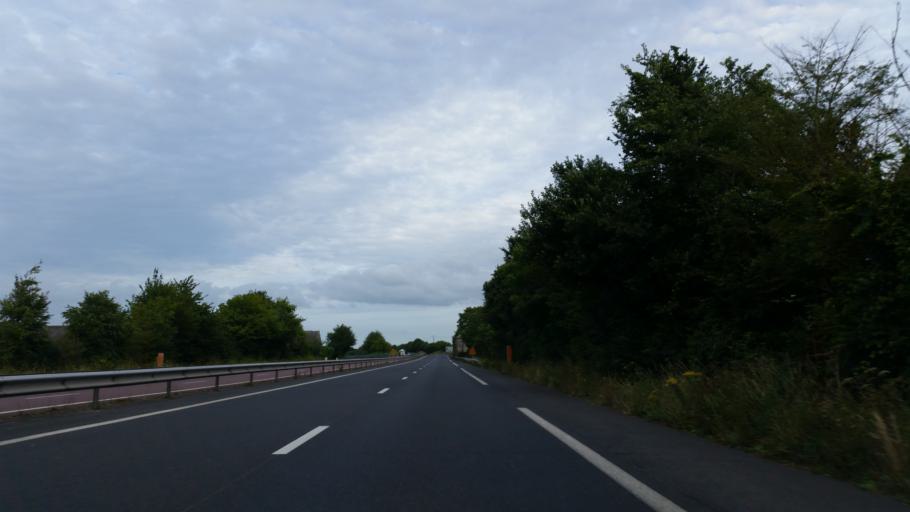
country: FR
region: Lower Normandy
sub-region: Departement du Calvados
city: Grandcamp-Maisy
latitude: 49.3427
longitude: -1.0380
